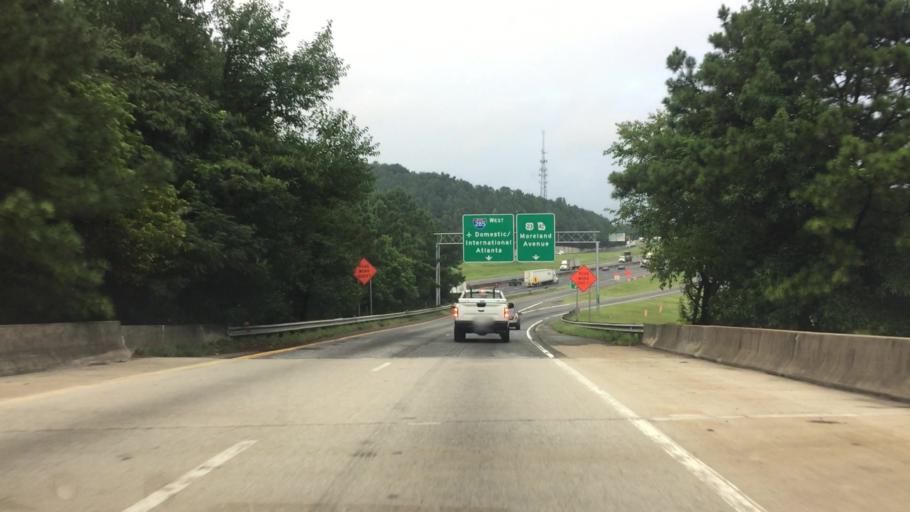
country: US
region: Georgia
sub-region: Clayton County
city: Conley
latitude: 33.6713
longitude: -84.3342
